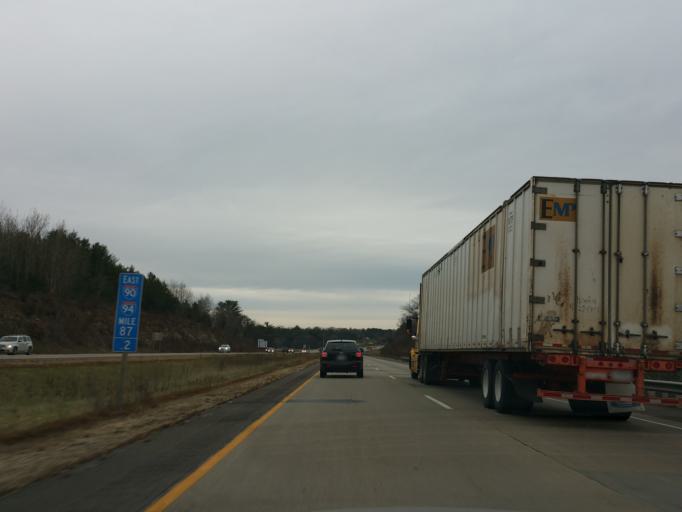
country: US
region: Wisconsin
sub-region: Sauk County
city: Lake Delton
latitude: 43.6318
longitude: -89.8074
